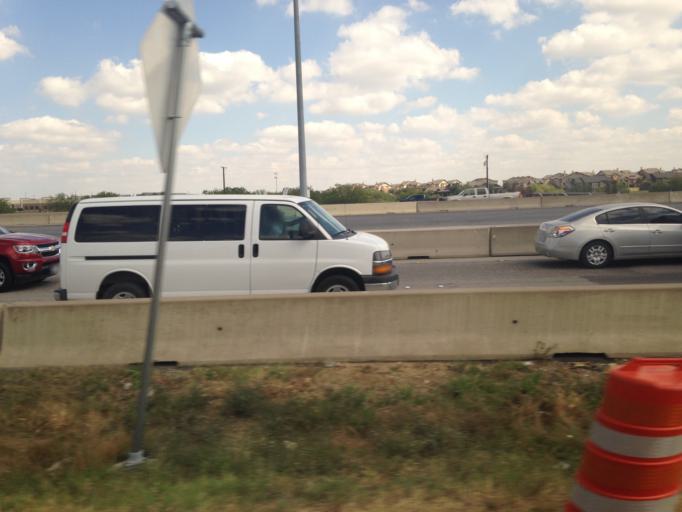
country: US
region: Texas
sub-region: Tarrant County
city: Blue Mound
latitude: 32.8960
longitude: -97.3177
